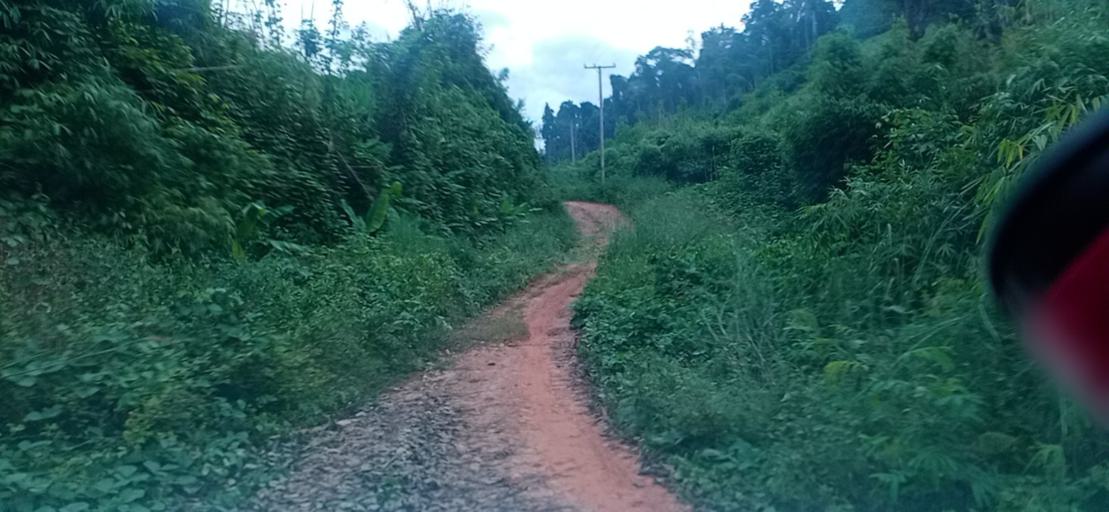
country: TH
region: Changwat Bueng Kan
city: Pak Khat
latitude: 18.5607
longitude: 103.2599
